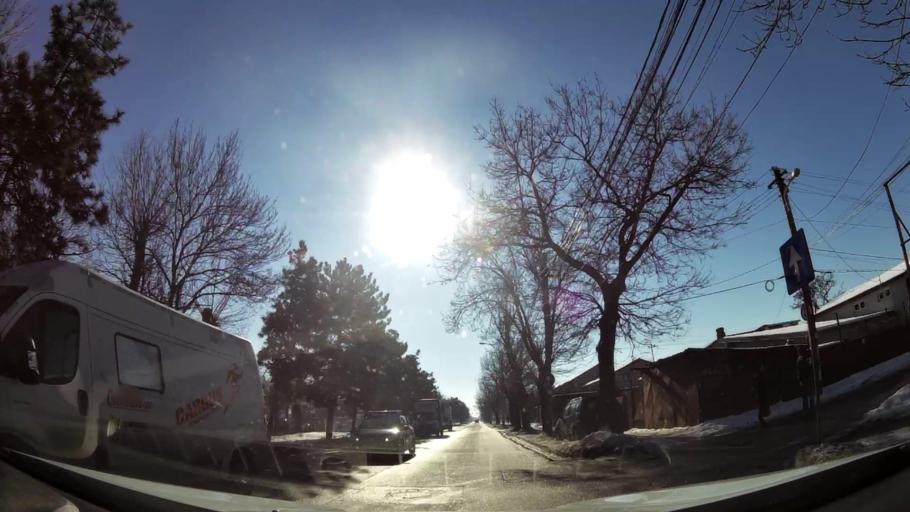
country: RO
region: Ilfov
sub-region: Comuna Magurele
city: Magurele
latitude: 44.3913
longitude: 26.0478
